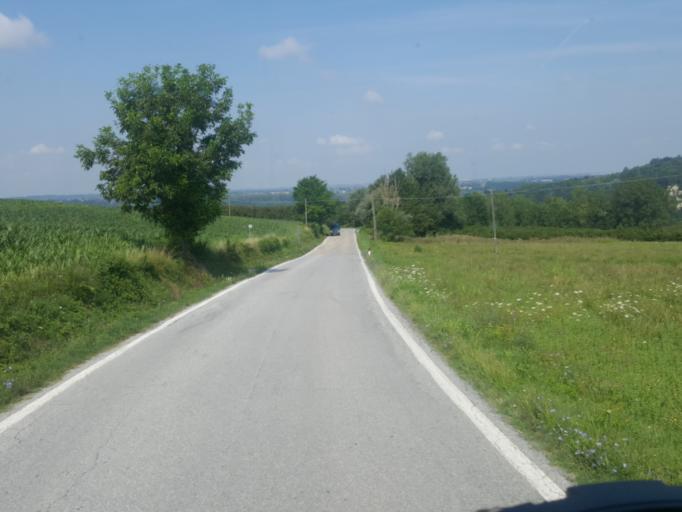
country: IT
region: Piedmont
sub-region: Provincia di Cuneo
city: Novello
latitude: 44.6068
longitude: 7.9107
